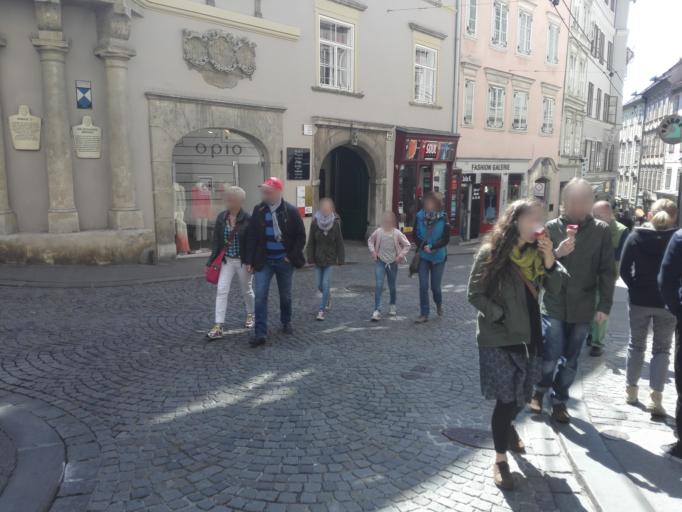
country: AT
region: Styria
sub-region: Graz Stadt
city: Graz
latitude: 47.0726
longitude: 15.4392
